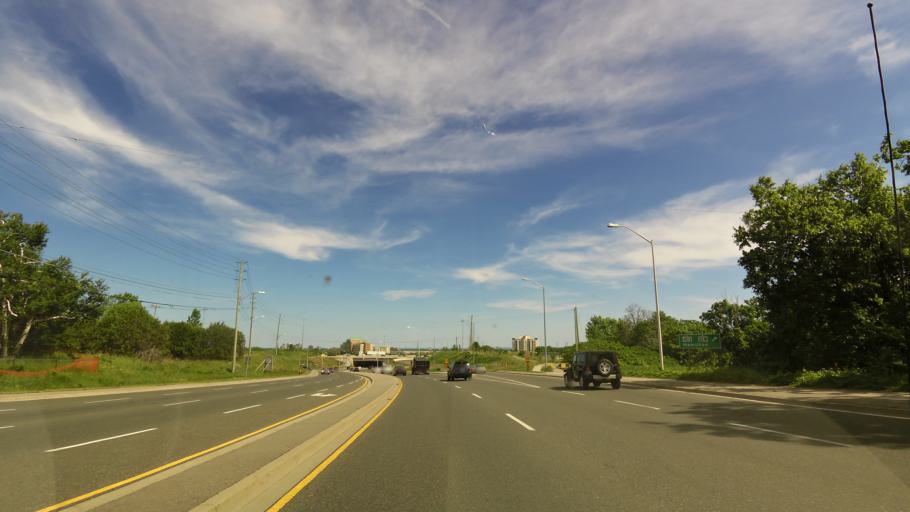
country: CA
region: Ontario
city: Oakville
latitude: 43.4124
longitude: -79.7441
